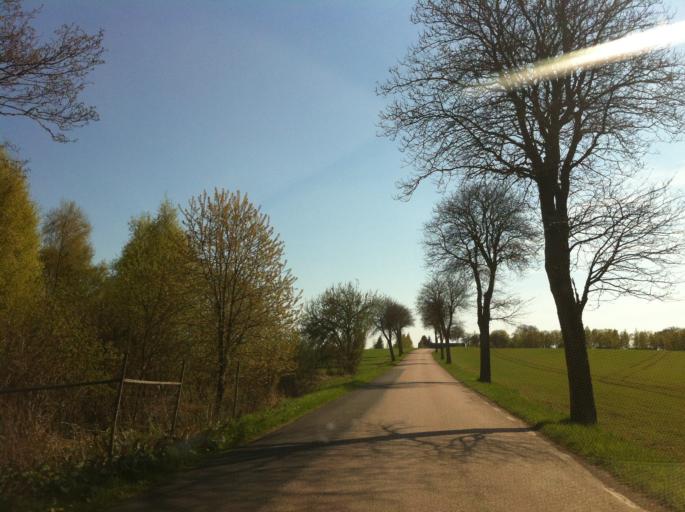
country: SE
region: Skane
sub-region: Svalovs Kommun
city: Kagerod
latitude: 56.0089
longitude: 13.0929
